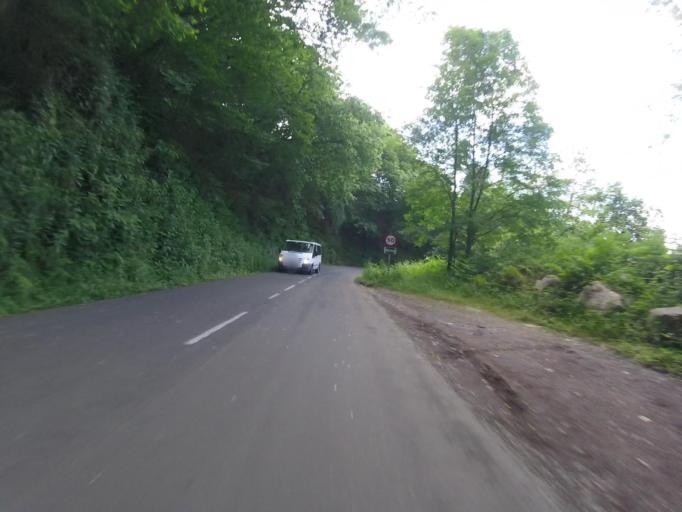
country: ES
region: Basque Country
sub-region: Provincia de Guipuzcoa
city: Errenteria
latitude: 43.2740
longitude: -1.8484
